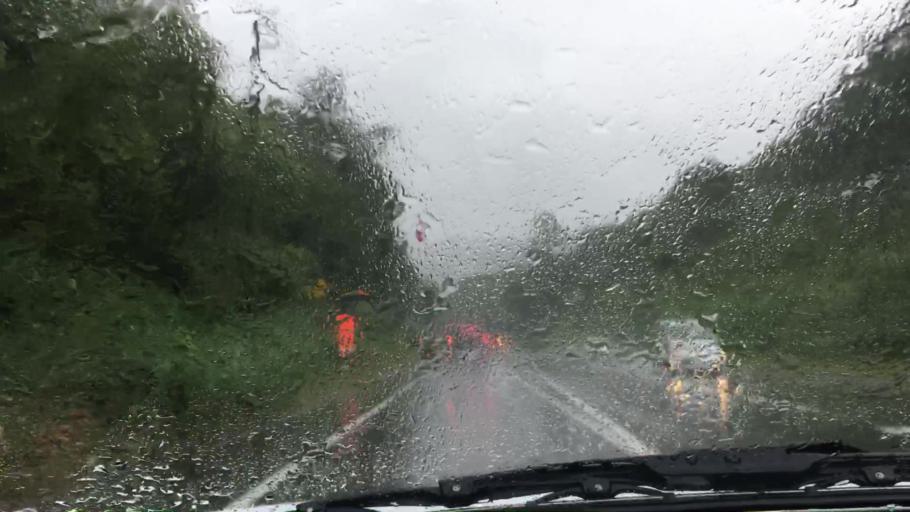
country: JP
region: Hokkaido
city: Sapporo
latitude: 42.8499
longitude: 141.0806
